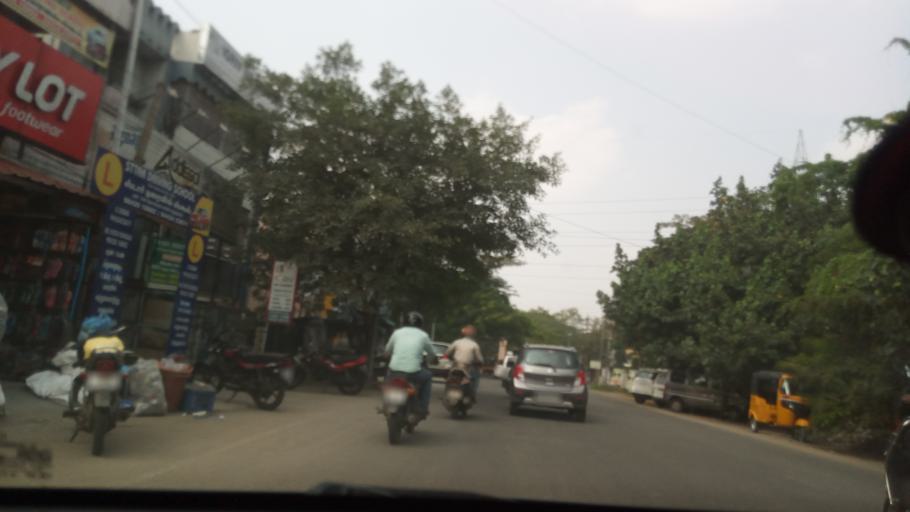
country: IN
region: Tamil Nadu
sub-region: Coimbatore
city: Coimbatore
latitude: 11.0180
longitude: 76.9581
